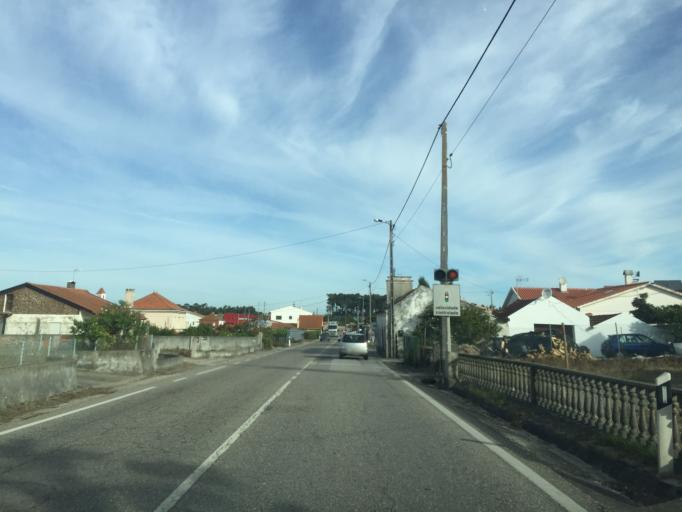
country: PT
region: Leiria
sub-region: Pombal
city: Lourical
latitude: 39.9822
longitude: -8.7988
